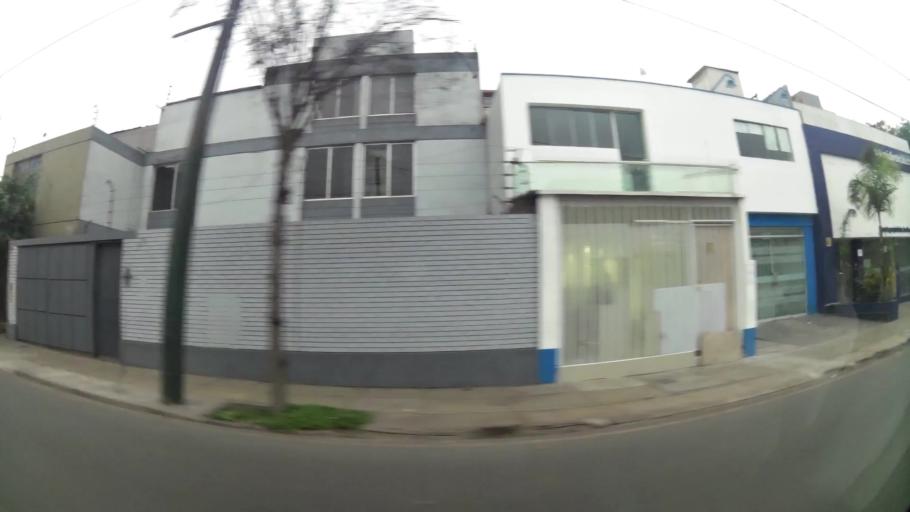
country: PE
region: Lima
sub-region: Lima
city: San Isidro
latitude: -12.0968
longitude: -77.0304
